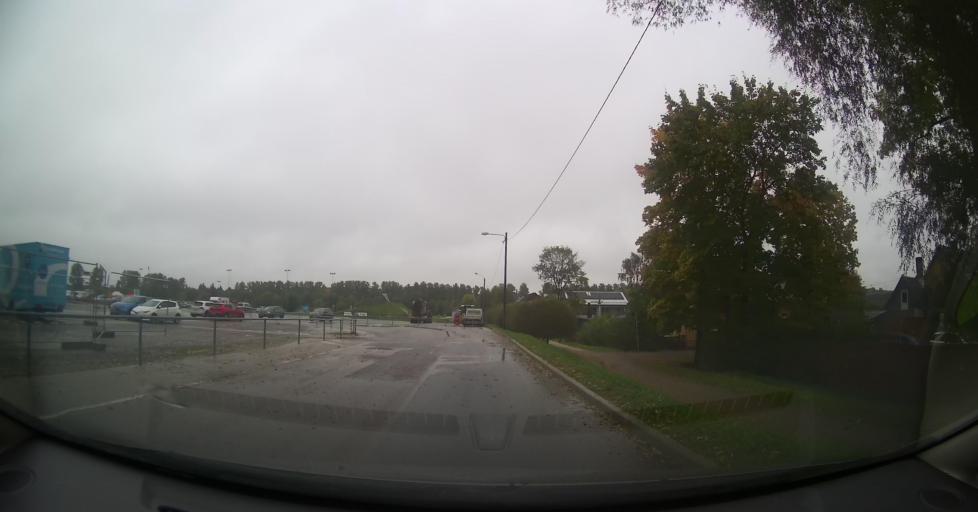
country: EE
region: Tartu
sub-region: Tartu linn
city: Tartu
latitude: 58.3880
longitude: 26.7048
